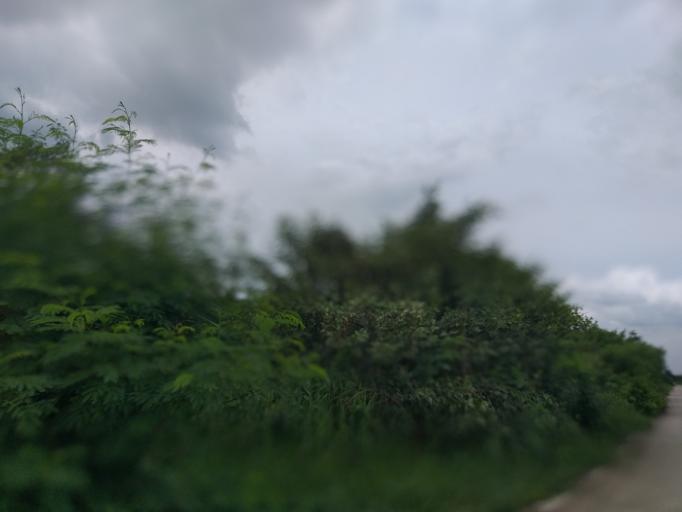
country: TH
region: Pathum Thani
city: Ban Lam Luk Ka
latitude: 13.9668
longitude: 100.8527
